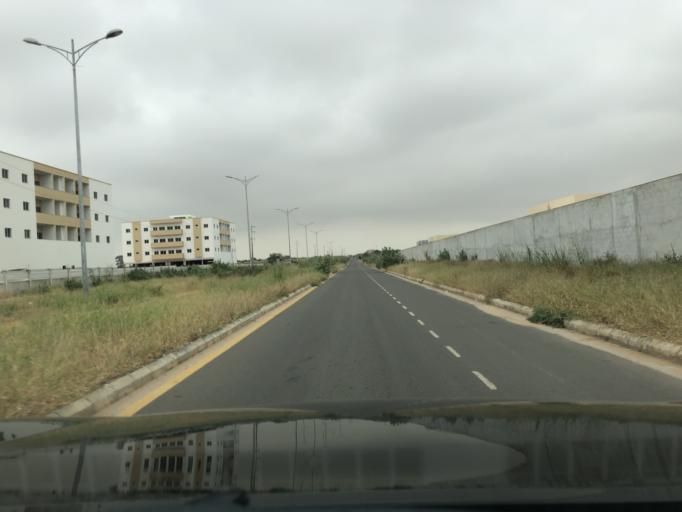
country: AO
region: Luanda
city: Luanda
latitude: -8.9547
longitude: 13.2567
